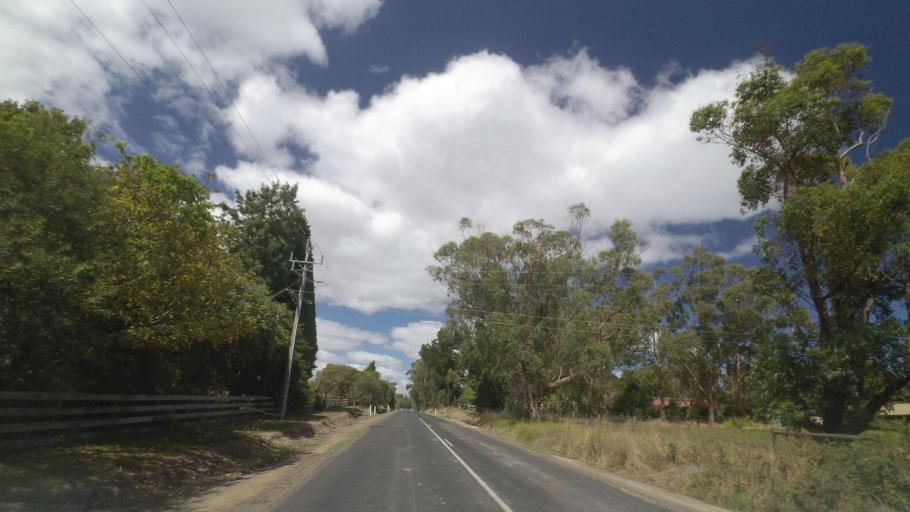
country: AU
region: Victoria
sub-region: Cardinia
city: Koo-Wee-Rup
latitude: -38.3272
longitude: 145.6708
